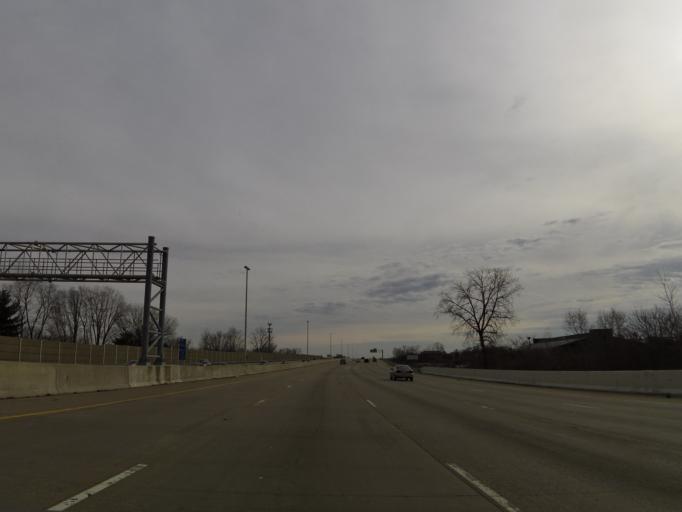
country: US
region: Indiana
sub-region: Marion County
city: Meridian Hills
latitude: 39.9298
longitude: -86.1419
